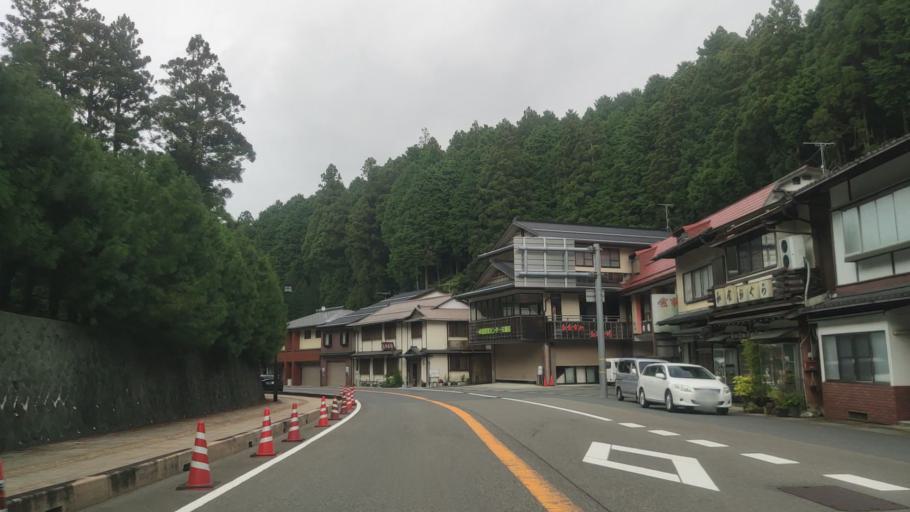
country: JP
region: Wakayama
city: Koya
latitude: 34.2144
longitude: 135.5981
